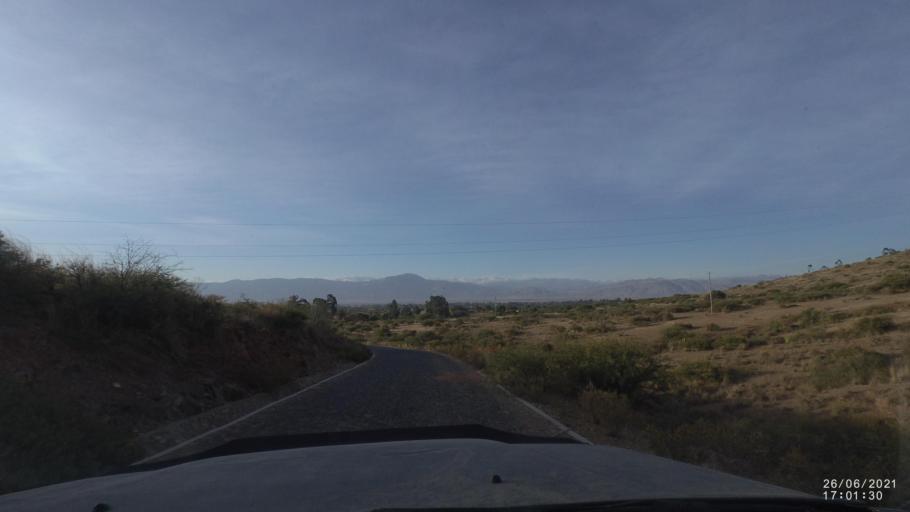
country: BO
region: Cochabamba
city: Cliza
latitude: -17.6605
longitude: -65.9108
